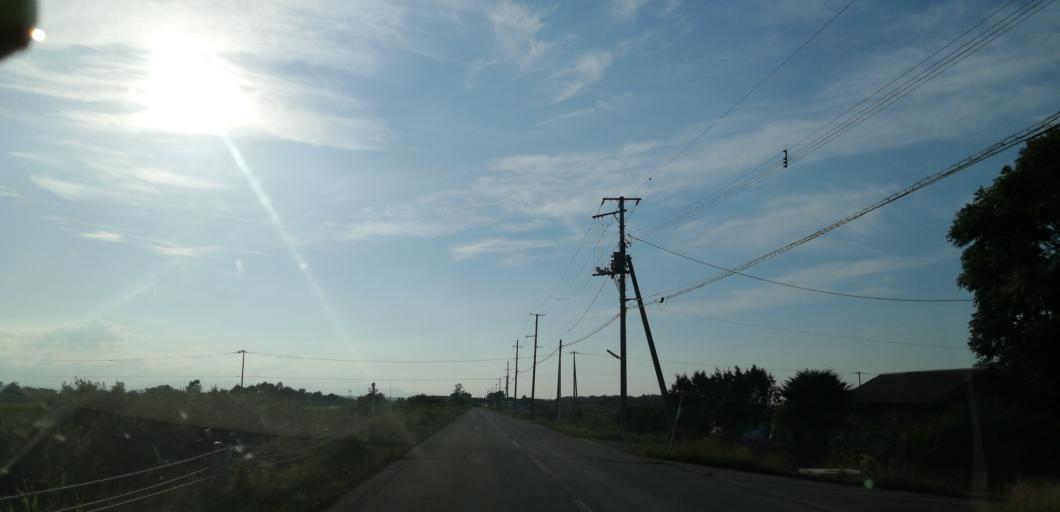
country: JP
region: Hokkaido
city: Kitahiroshima
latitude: 42.9593
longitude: 141.6458
